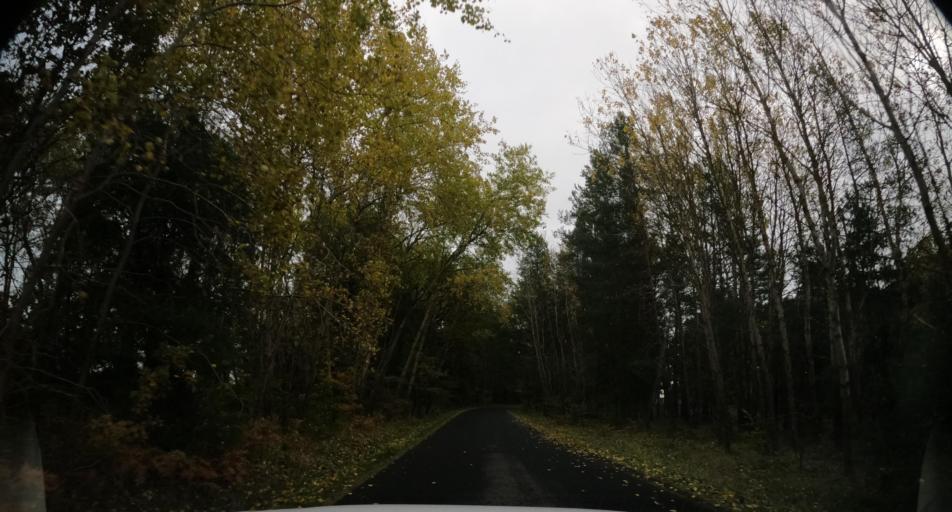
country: PL
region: West Pomeranian Voivodeship
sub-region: Powiat kamienski
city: Wolin
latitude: 53.9192
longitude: 14.5577
